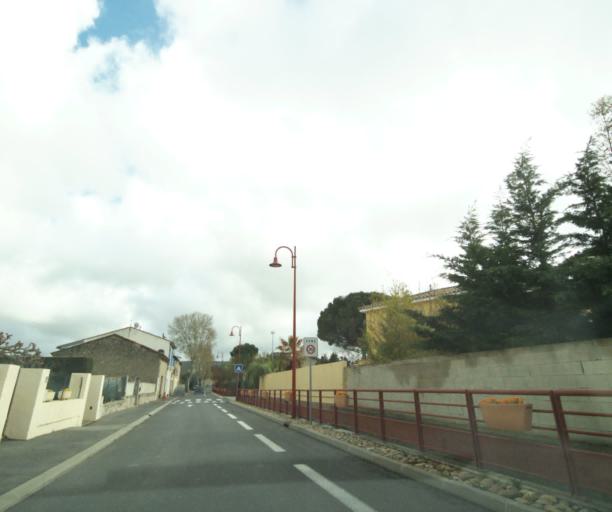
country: FR
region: Languedoc-Roussillon
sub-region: Departement de l'Herault
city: Fabregues
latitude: 43.5565
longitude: 3.7760
